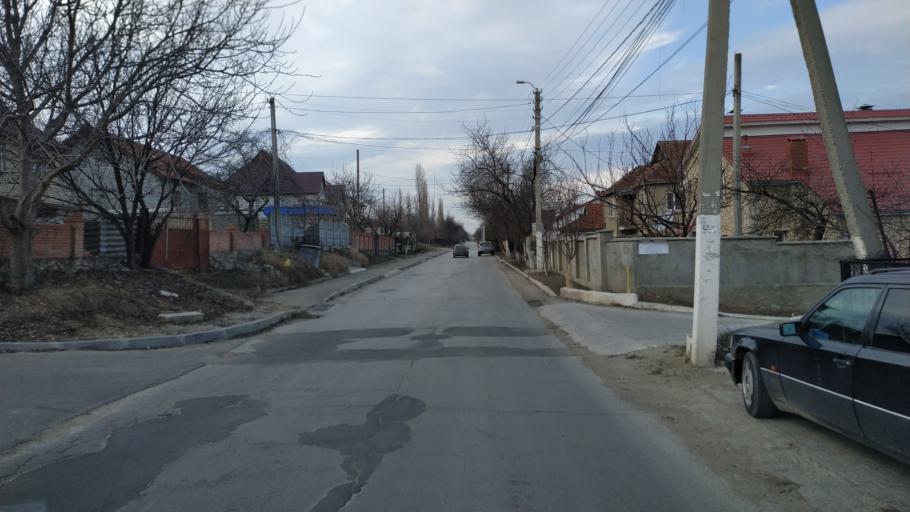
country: MD
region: Laloveni
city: Ialoveni
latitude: 46.9561
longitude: 28.7602
